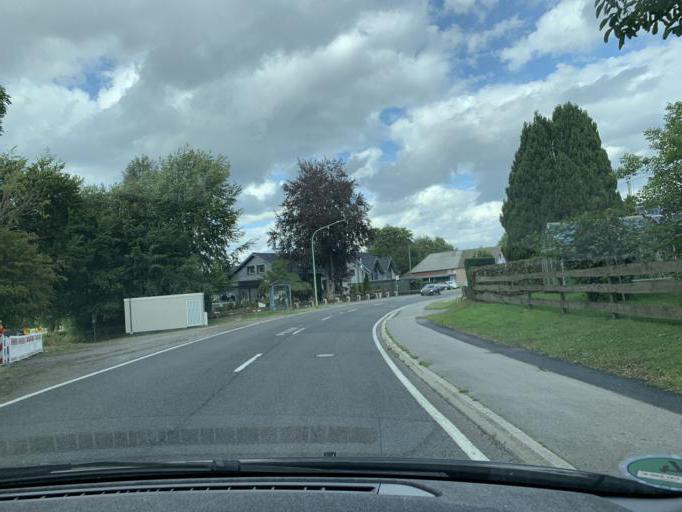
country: DE
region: North Rhine-Westphalia
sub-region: Regierungsbezirk Koln
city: Simmerath
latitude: 50.6209
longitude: 6.3197
